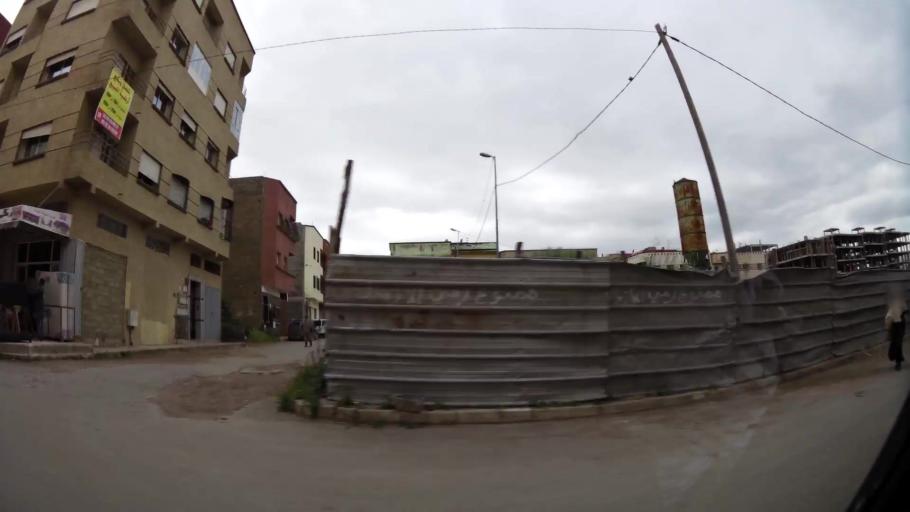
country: MA
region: Grand Casablanca
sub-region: Mediouna
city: Tit Mellil
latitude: 33.5568
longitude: -7.5319
